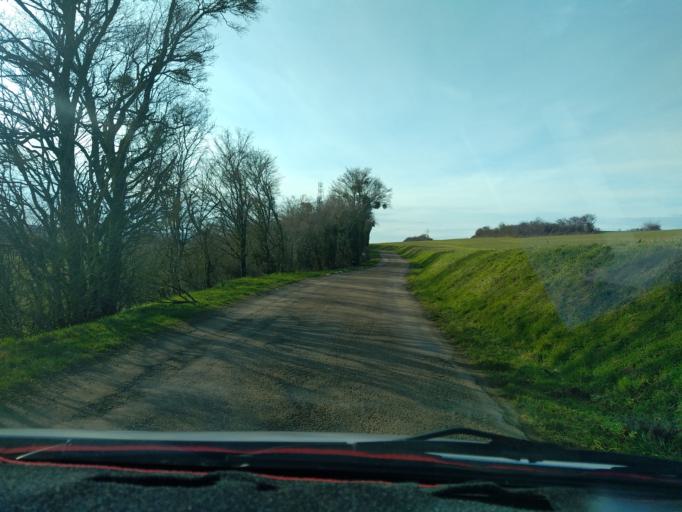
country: FR
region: Franche-Comte
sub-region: Departement de la Haute-Saone
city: Marnay
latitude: 47.3127
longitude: 5.6780
